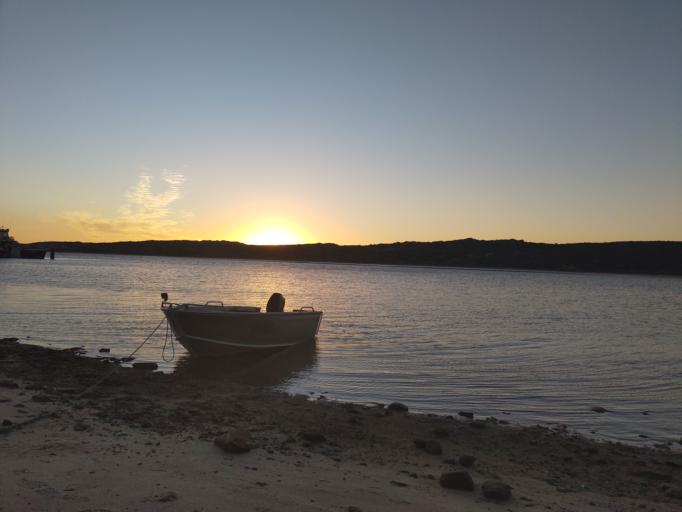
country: AU
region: Western Australia
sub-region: Northampton Shire
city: Kalbarri
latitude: -27.6990
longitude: 114.1688
